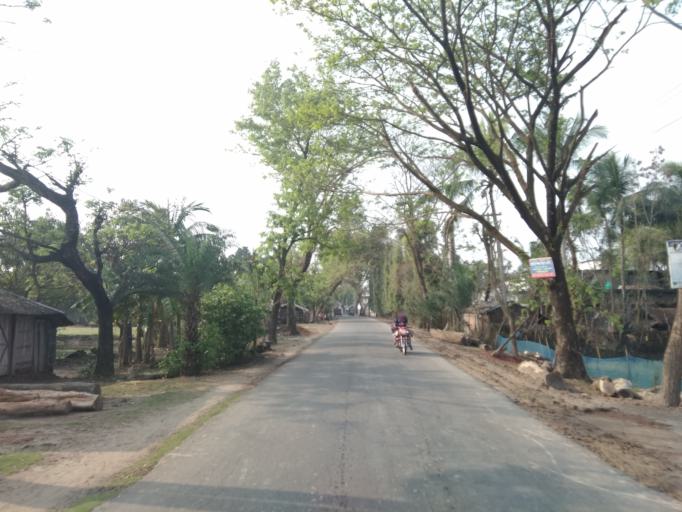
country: IN
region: West Bengal
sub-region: North 24 Parganas
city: Taki
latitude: 22.3281
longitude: 89.1055
